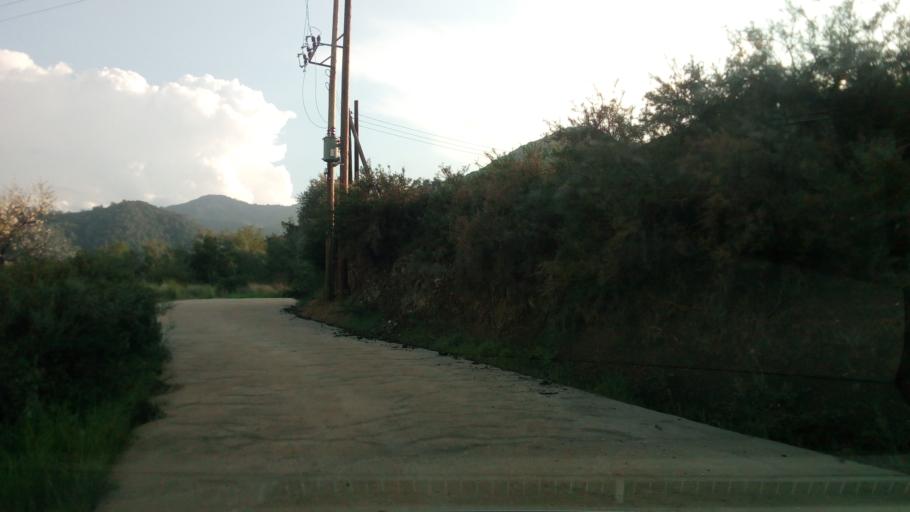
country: CY
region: Lefkosia
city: Kato Pyrgos
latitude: 35.1721
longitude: 32.6689
